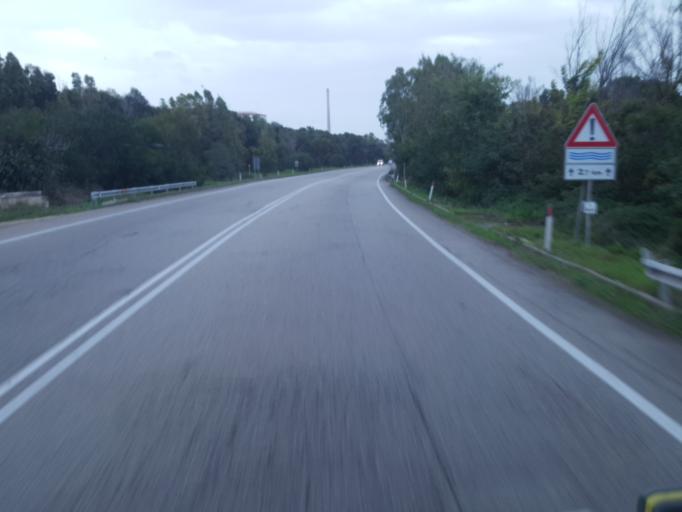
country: IT
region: Apulia
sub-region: Provincia di Taranto
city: Statte
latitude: 40.5133
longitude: 17.1890
